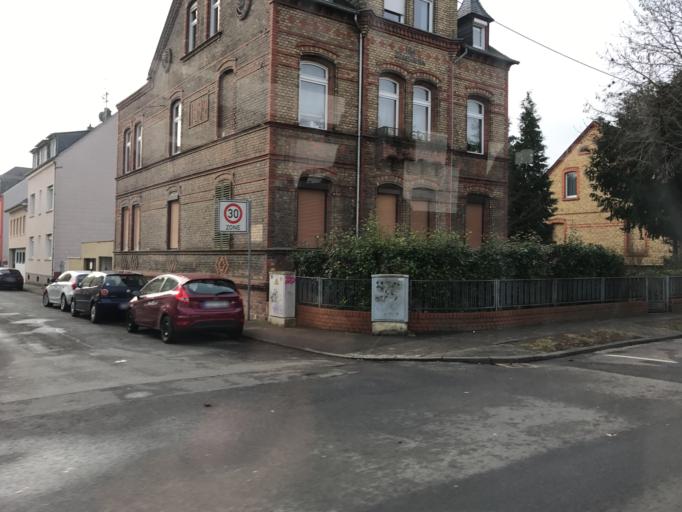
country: DE
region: Rheinland-Pfalz
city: Budenheim
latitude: 50.0446
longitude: 8.2006
